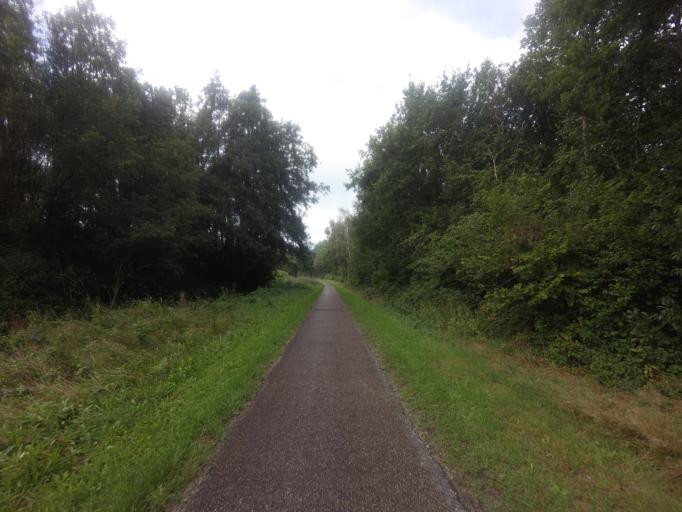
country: NL
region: Friesland
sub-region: Gemeente Heerenveen
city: De Knipe
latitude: 52.9564
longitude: 6.0068
